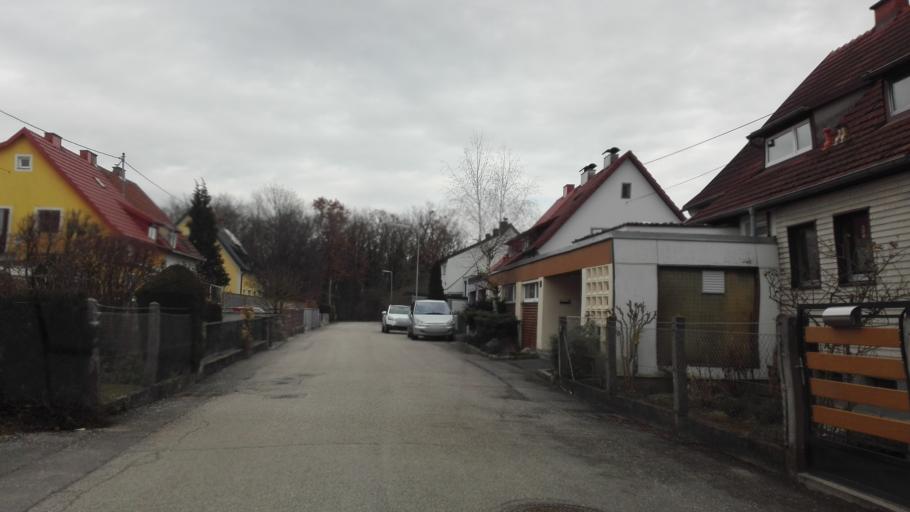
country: AT
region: Upper Austria
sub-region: Politischer Bezirk Linz-Land
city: Traun
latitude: 48.2484
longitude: 14.2485
